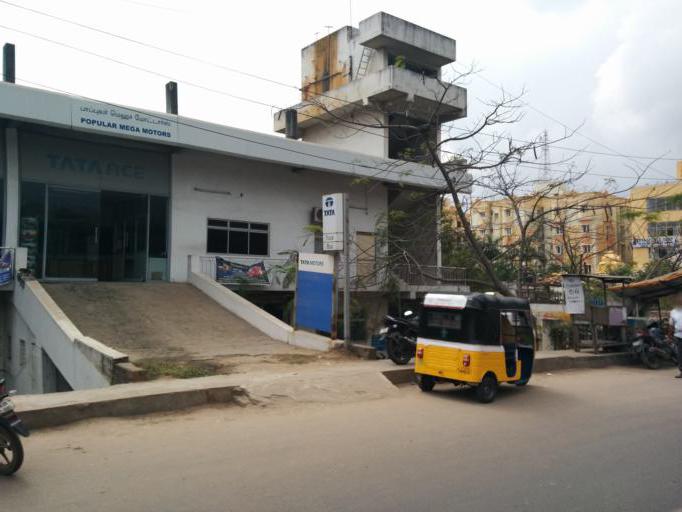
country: IN
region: Tamil Nadu
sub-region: Thiruvallur
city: Ambattur
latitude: 13.0674
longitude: 80.1776
